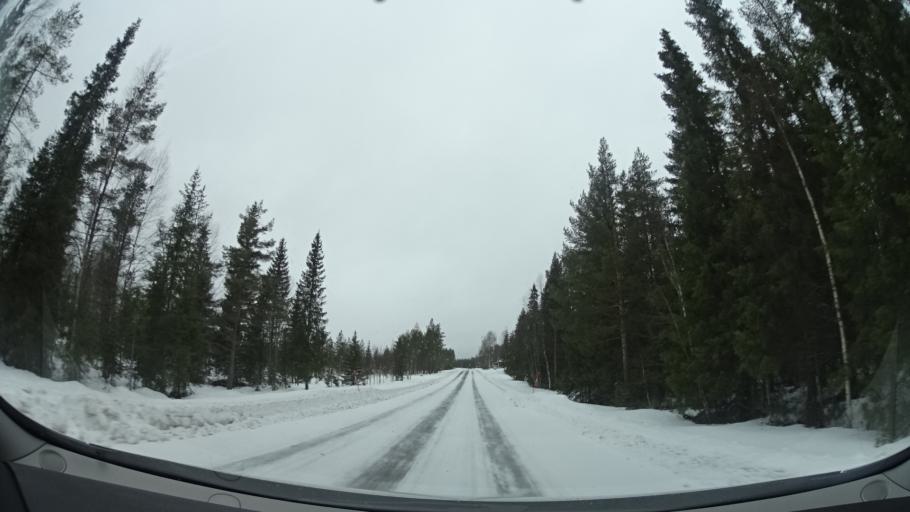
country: SE
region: Vaesterbotten
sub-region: Mala Kommun
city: Mala
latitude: 65.0808
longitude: 19.0024
